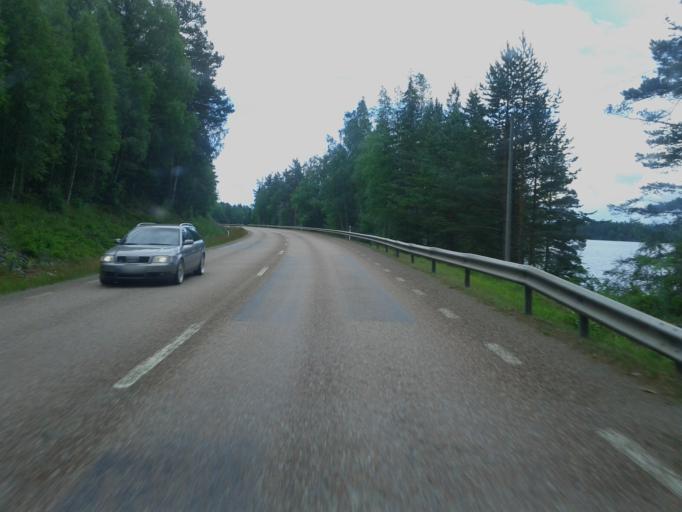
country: SE
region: Dalarna
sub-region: Faluns Kommun
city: Bjursas
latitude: 60.7621
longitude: 15.3218
